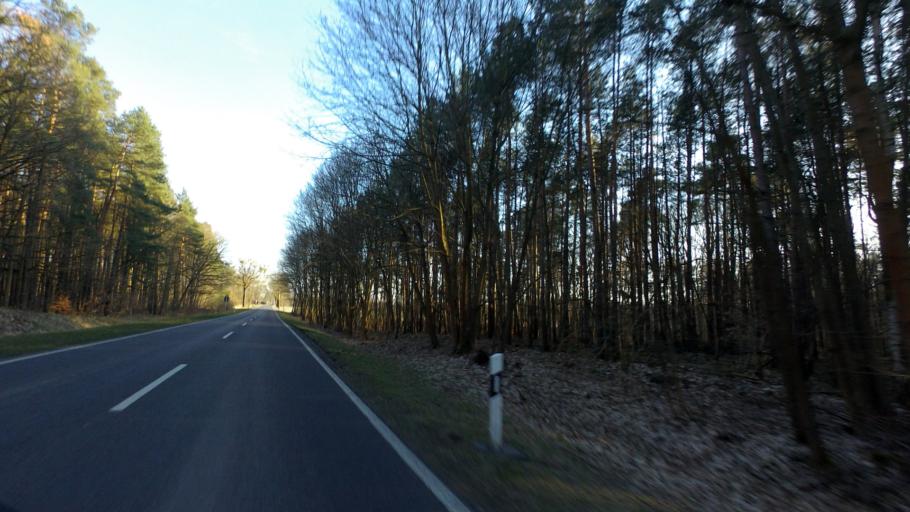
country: DE
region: Brandenburg
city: Eberswalde
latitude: 52.7892
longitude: 13.8383
